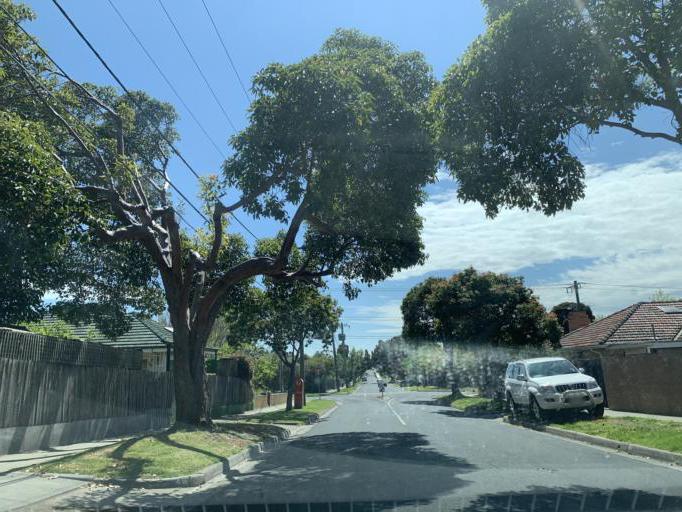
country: AU
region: Victoria
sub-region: Bayside
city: Moorabbin
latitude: -37.9445
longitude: 145.0326
